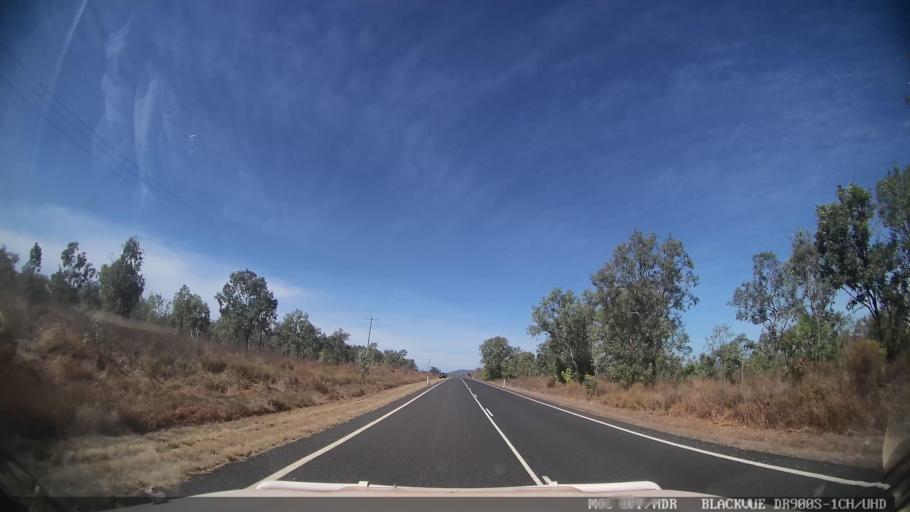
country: AU
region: Queensland
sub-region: Cook
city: Cooktown
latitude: -15.8656
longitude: 144.8121
